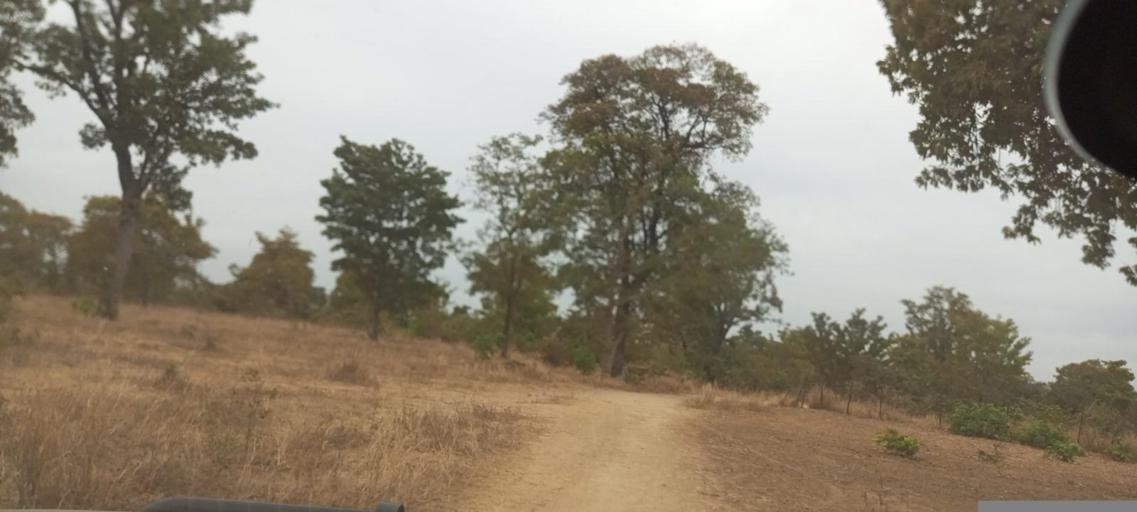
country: ML
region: Koulikoro
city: Kati
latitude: 12.7701
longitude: -8.3726
